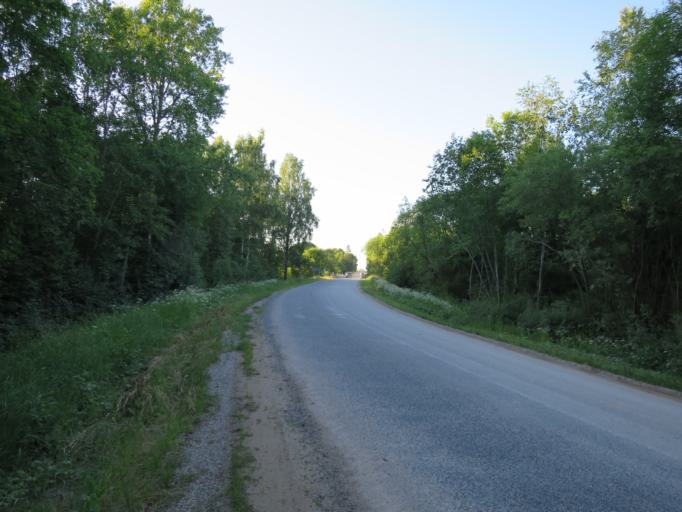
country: LV
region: Rucavas
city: Rucava
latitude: 56.3305
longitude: 21.3090
